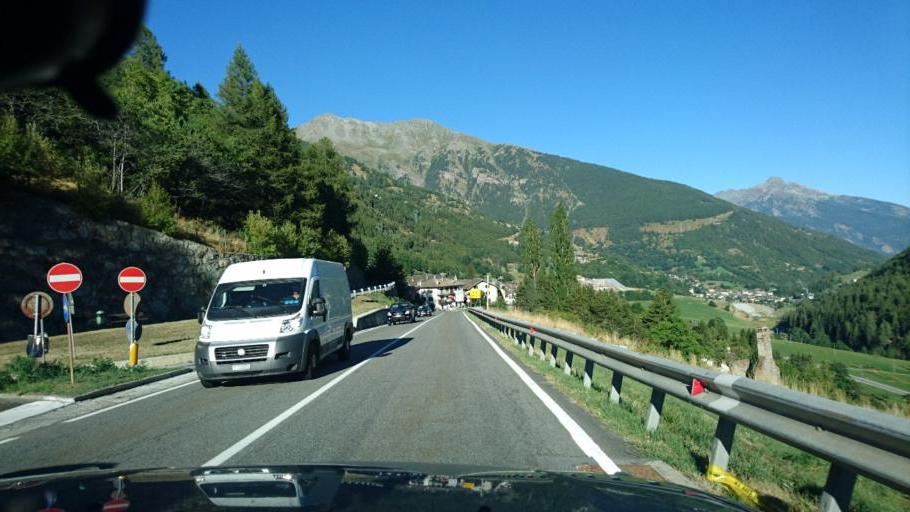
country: IT
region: Aosta Valley
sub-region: Valle d'Aosta
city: Saint-Oyen
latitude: 45.8235
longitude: 7.2062
